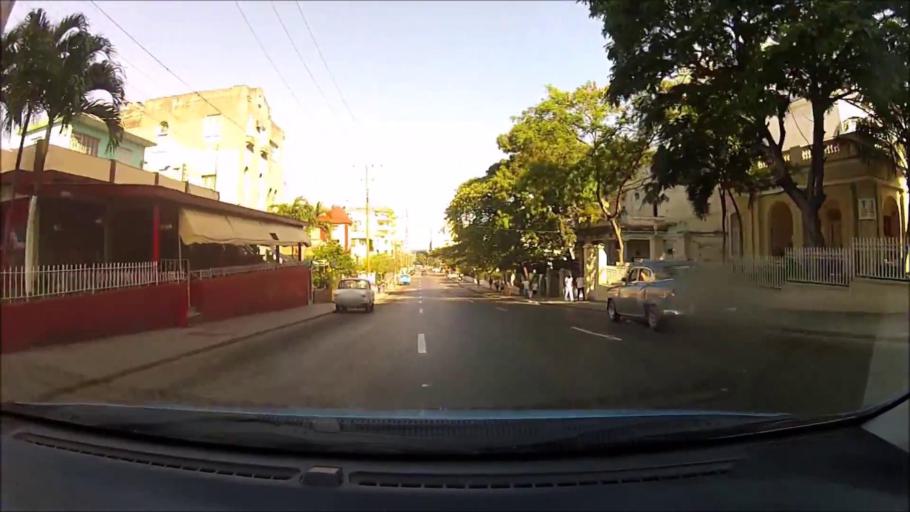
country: CU
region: La Habana
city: Havana
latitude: 23.1408
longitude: -82.3844
